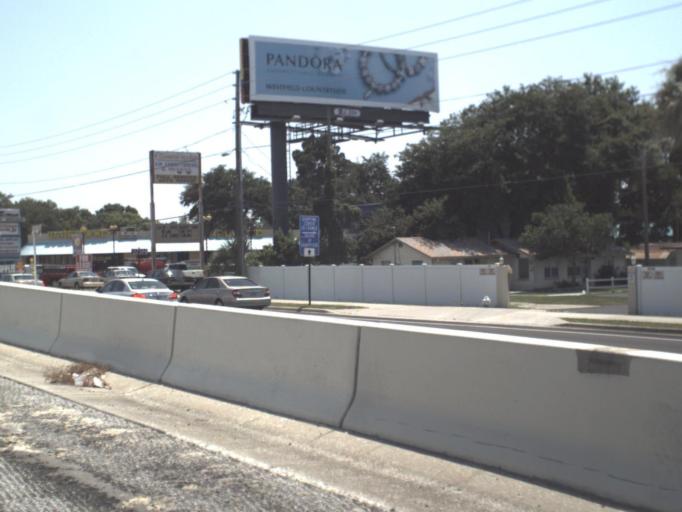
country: US
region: Florida
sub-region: Pinellas County
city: Dunedin
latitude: 28.0218
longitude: -82.7382
